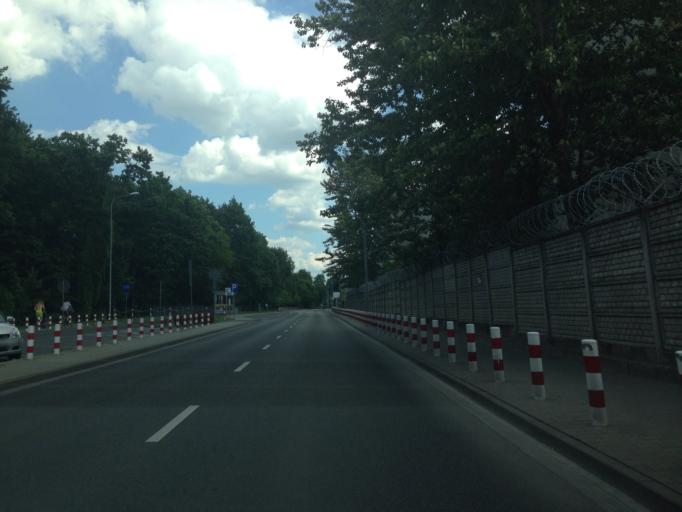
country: PL
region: Masovian Voivodeship
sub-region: Warszawa
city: Bemowo
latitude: 52.2508
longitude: 20.8881
